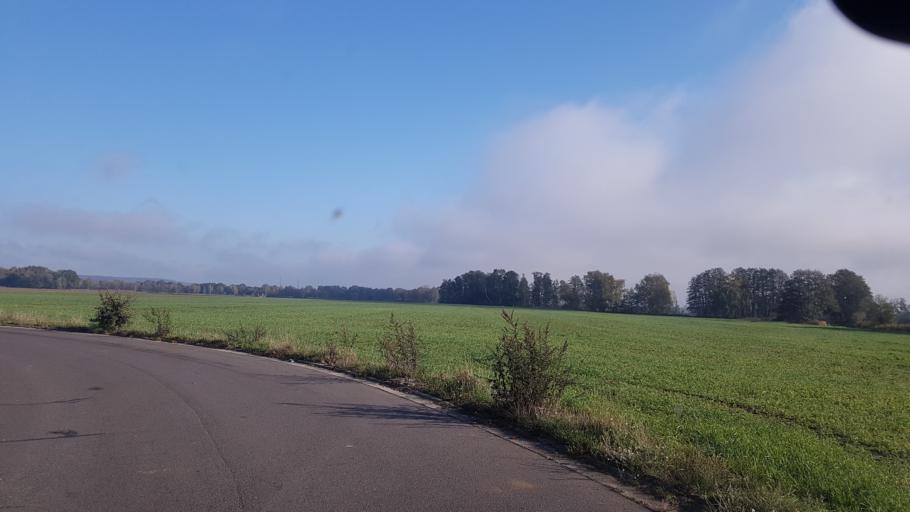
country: DE
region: Brandenburg
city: Elsterwerda
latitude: 51.4609
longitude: 13.5478
